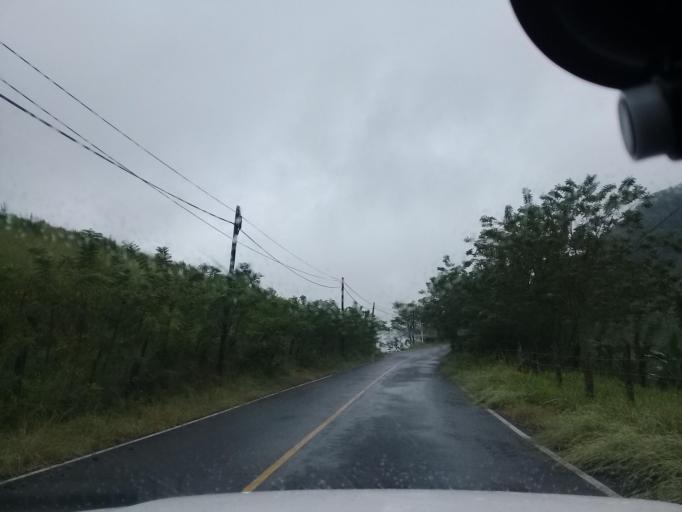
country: MX
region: Veracruz
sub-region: Chalma
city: San Pedro Coyutla
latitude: 21.2304
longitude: -98.4516
